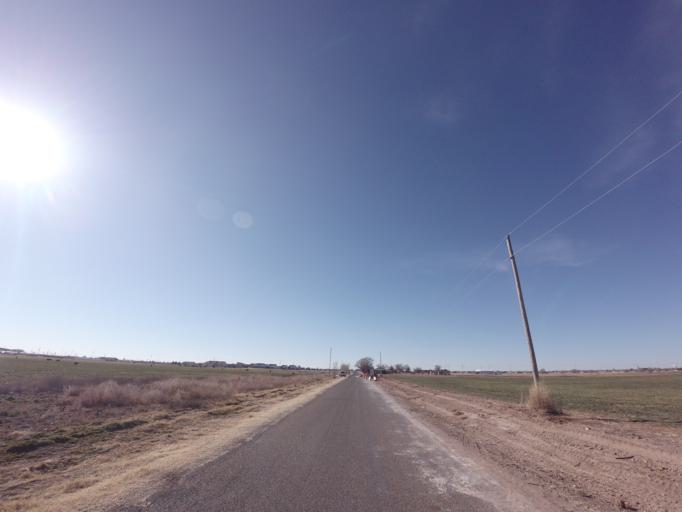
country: US
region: New Mexico
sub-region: Curry County
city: Clovis
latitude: 34.4049
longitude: -103.1571
